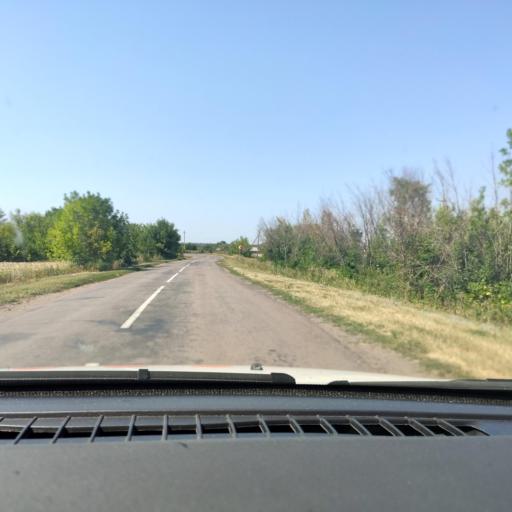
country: RU
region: Voronezj
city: Imeni Pervogo Maya
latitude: 50.7164
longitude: 39.3952
